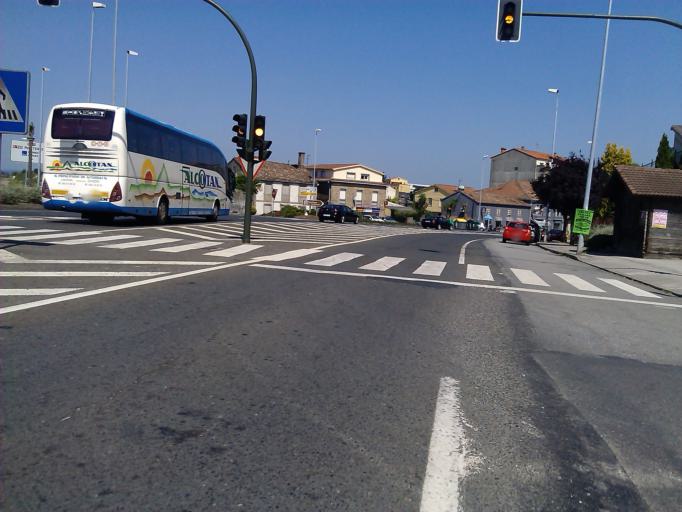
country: ES
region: Galicia
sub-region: Provincia da Coruna
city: Santiago de Compostela
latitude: 42.8596
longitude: -8.5397
